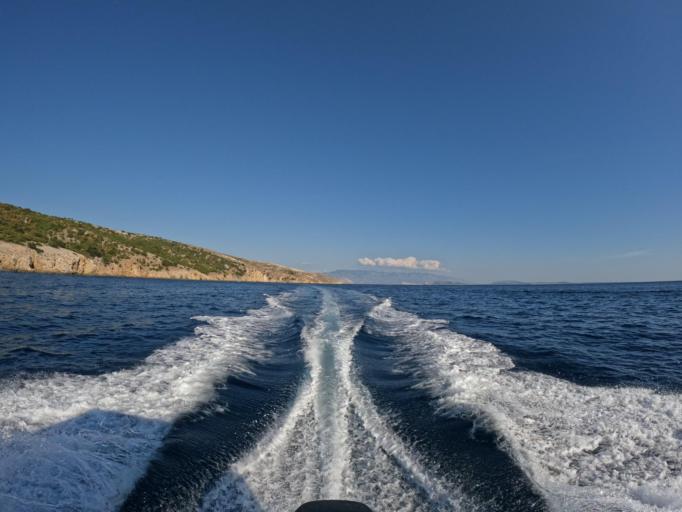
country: HR
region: Primorsko-Goranska
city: Punat
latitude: 44.9758
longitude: 14.6211
